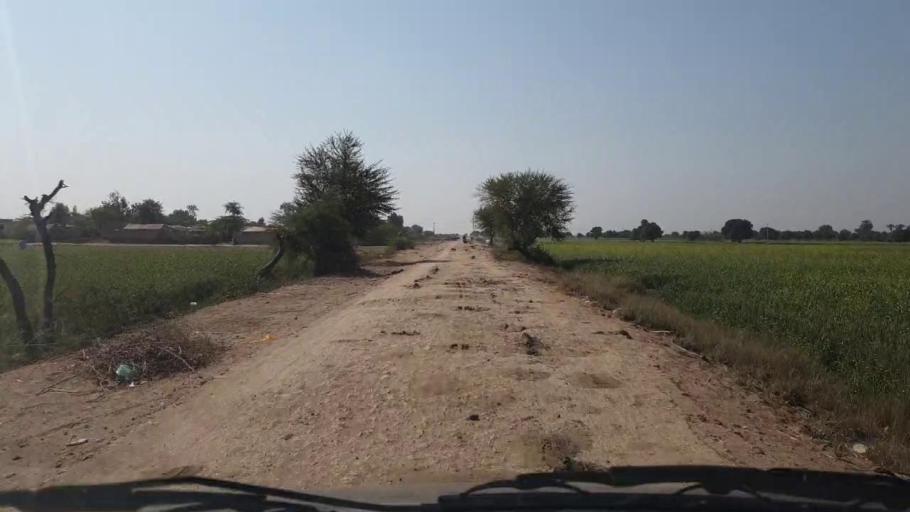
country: PK
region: Sindh
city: Samaro
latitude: 25.2737
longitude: 69.2518
